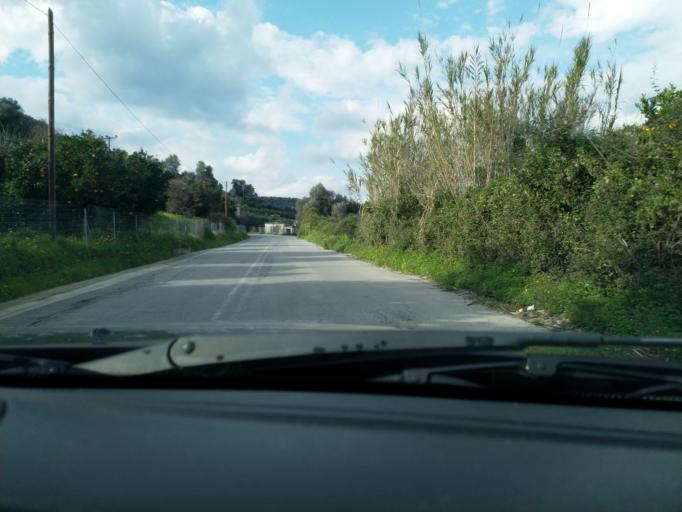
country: GR
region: Crete
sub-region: Nomos Chanias
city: Gerani
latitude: 35.4999
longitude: 23.8992
